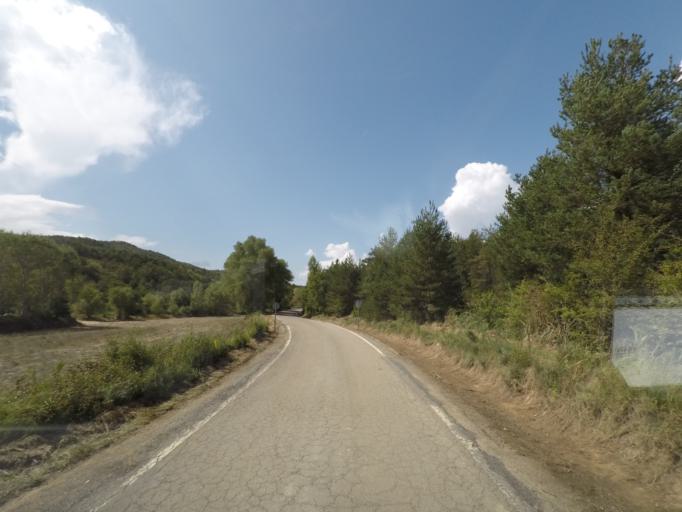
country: ES
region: Aragon
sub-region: Provincia de Huesca
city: Arguis
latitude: 42.4029
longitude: -0.3788
